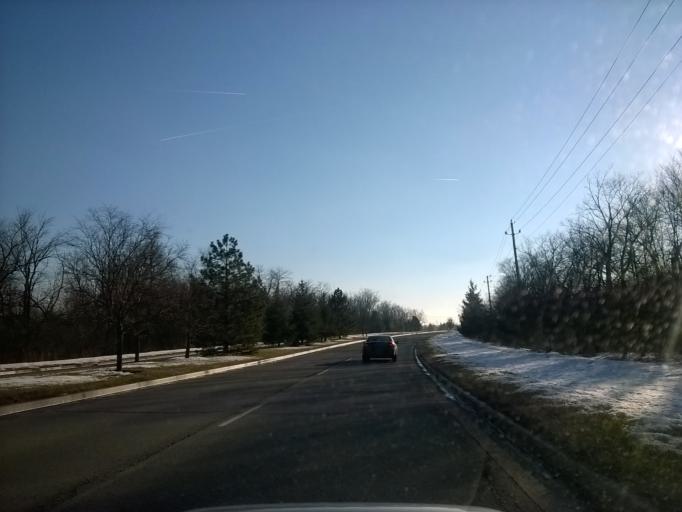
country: US
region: Indiana
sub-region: Hamilton County
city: Carmel
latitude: 39.9450
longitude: -86.0730
